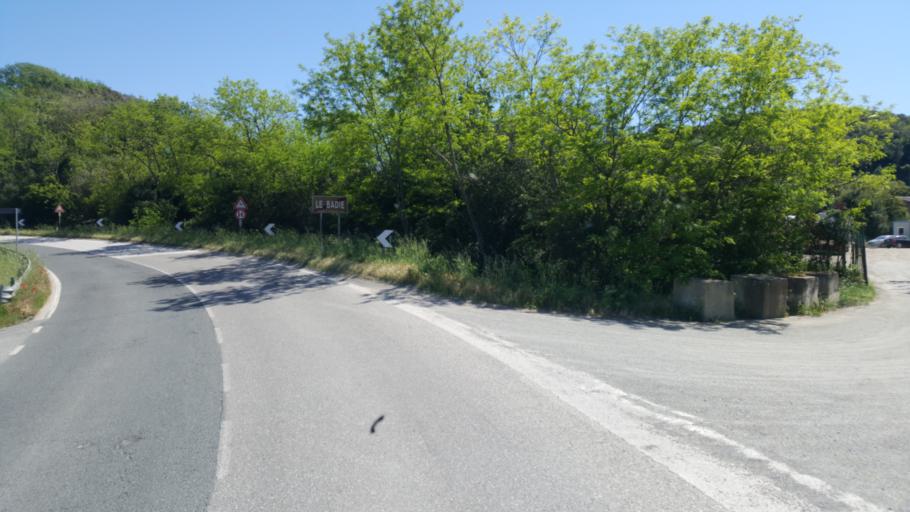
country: IT
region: Tuscany
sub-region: Provincia di Livorno
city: Rosignano Marittimo
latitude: 43.3964
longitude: 10.4959
